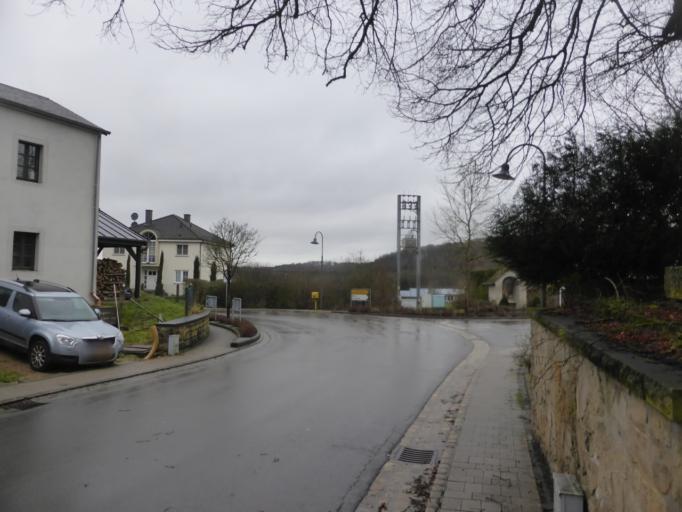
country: LU
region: Luxembourg
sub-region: Canton de Mersch
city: Lorentzweiler
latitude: 49.7021
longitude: 6.1654
